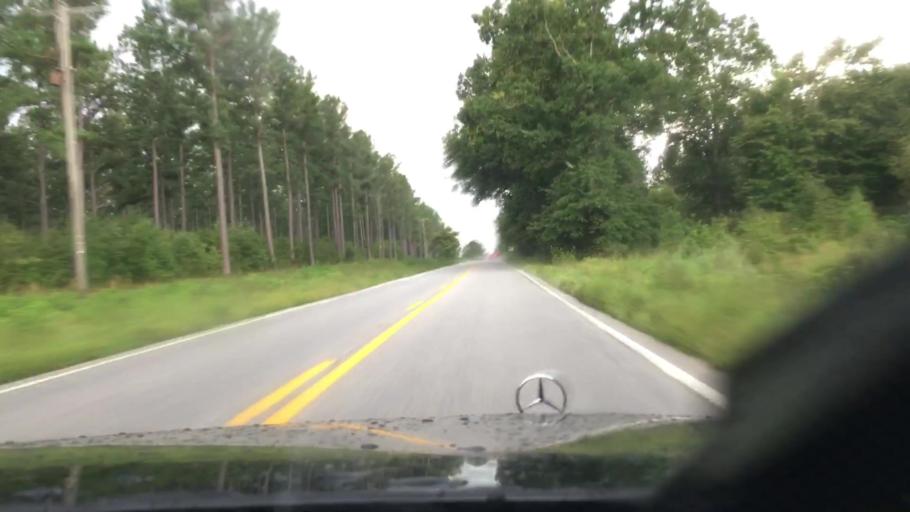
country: US
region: Virginia
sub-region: Nelson County
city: Lovingston
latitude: 37.7455
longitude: -78.9960
